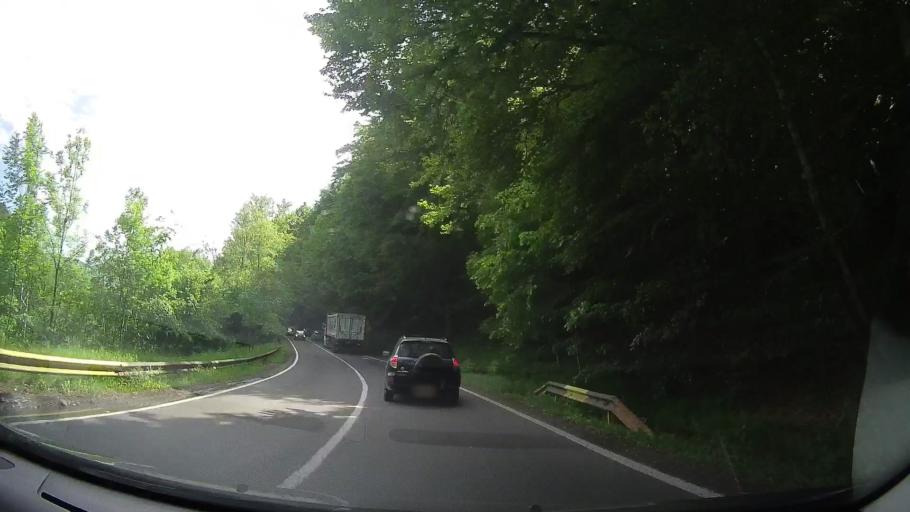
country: RO
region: Prahova
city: Maneciu
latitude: 45.3889
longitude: 25.9299
